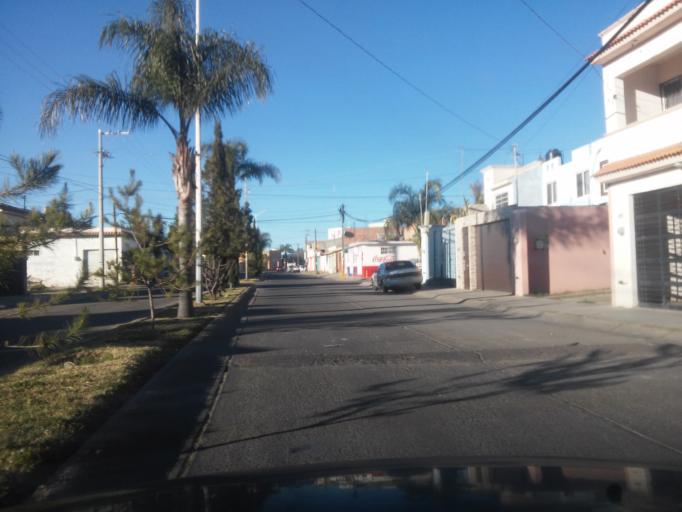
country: MX
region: Durango
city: Victoria de Durango
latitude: 24.0021
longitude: -104.6402
